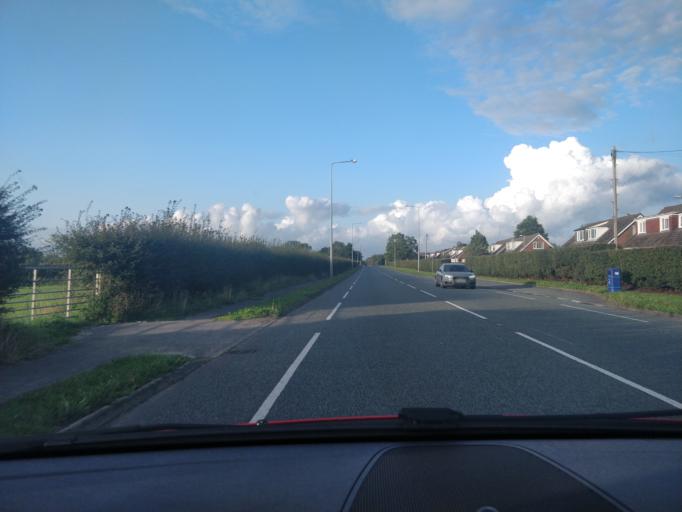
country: GB
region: England
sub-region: Lancashire
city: Tarleton
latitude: 53.7006
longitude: -2.8060
